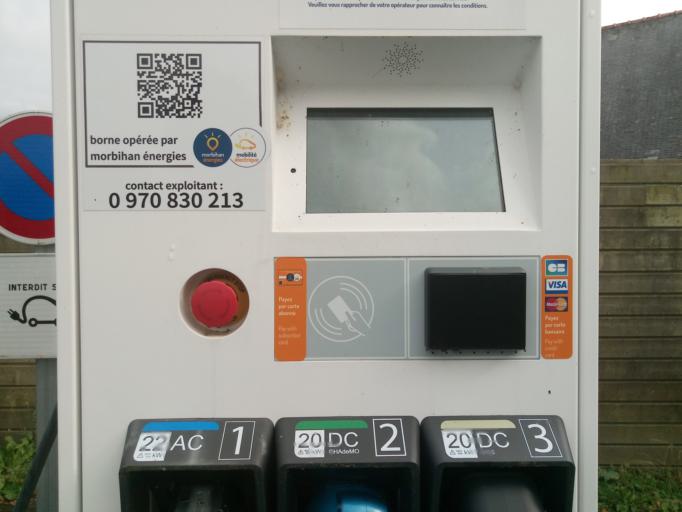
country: FR
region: Brittany
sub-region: Departement du Morbihan
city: Gourin
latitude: 48.1411
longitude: -3.6009
